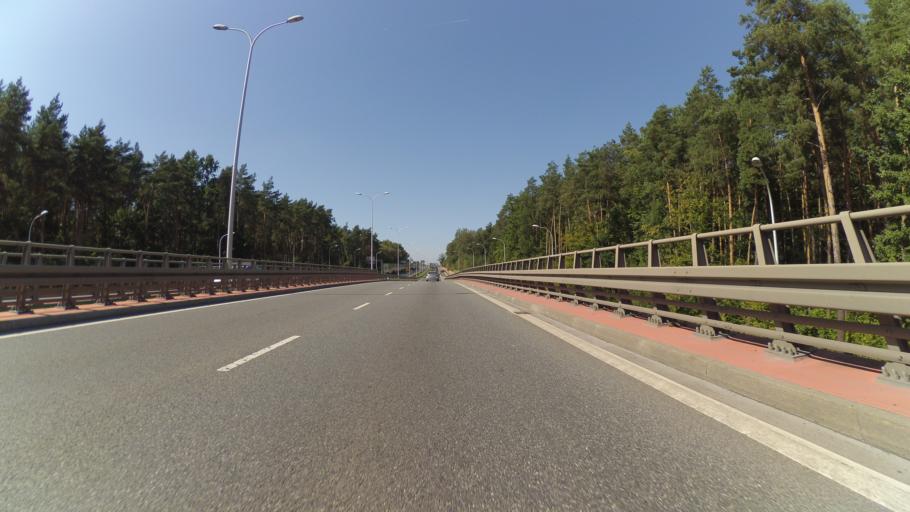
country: PL
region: Podlasie
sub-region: Bialystok
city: Bialystok
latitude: 53.1594
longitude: 23.1406
